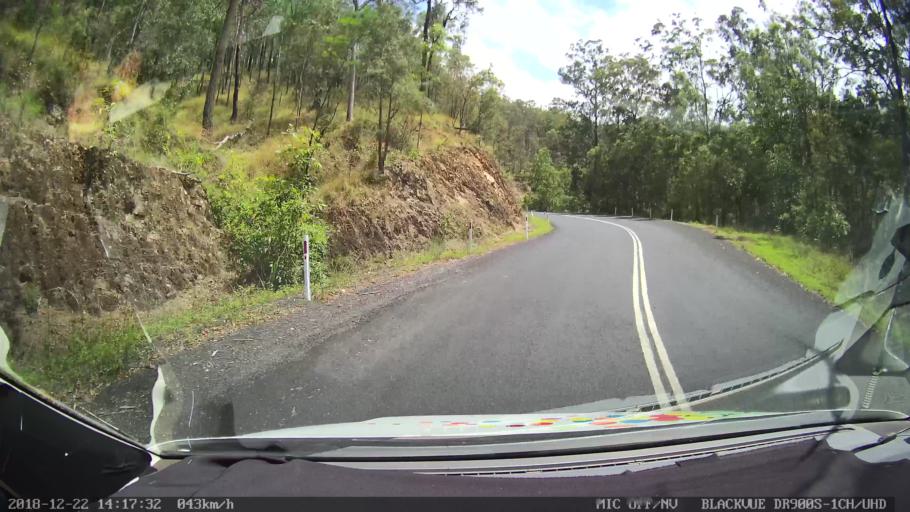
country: AU
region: New South Wales
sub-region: Clarence Valley
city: Coutts Crossing
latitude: -30.0089
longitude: 152.6685
